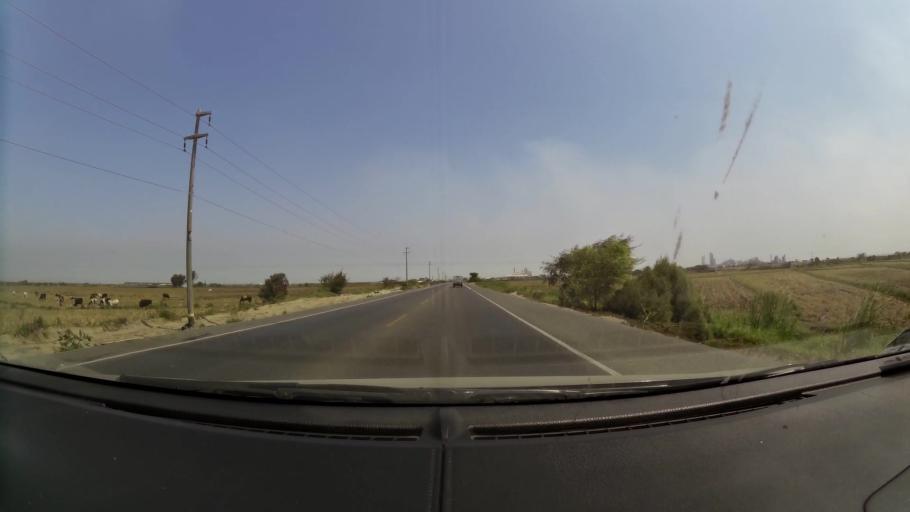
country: PE
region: La Libertad
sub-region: Provincia de Pacasmayo
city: San Pedro de Lloc
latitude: -7.4190
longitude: -79.5350
